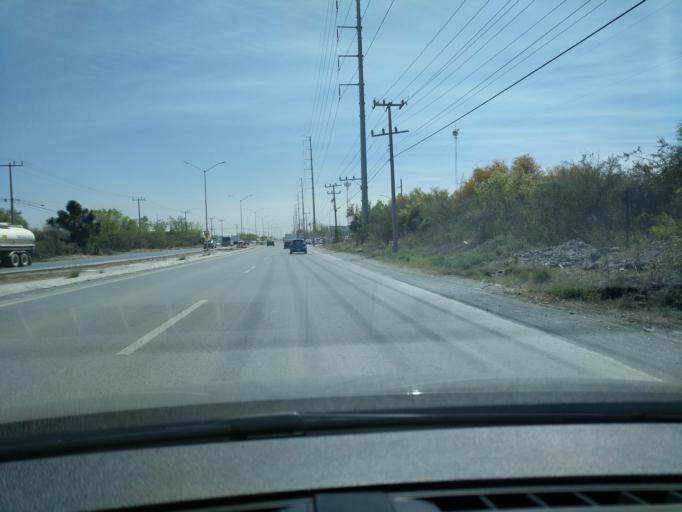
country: MX
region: Nuevo Leon
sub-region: Salinas Victoria
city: Emiliano Zapata
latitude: 25.9065
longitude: -100.2654
